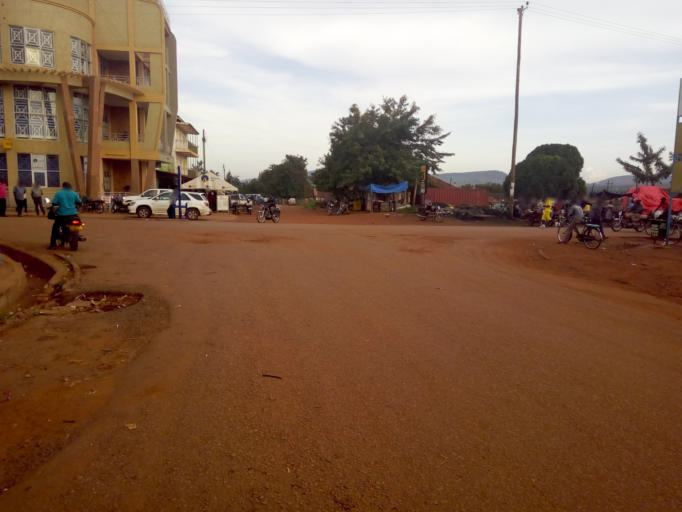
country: UG
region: Western Region
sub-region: Masindi District
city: Masindi
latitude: 1.6821
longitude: 31.7228
